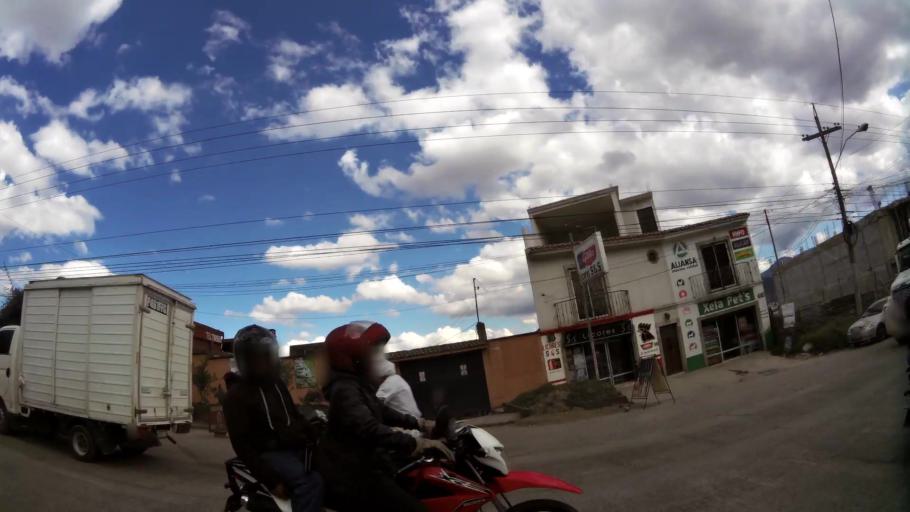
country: GT
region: Quetzaltenango
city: Quetzaltenango
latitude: 14.8419
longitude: -91.5356
